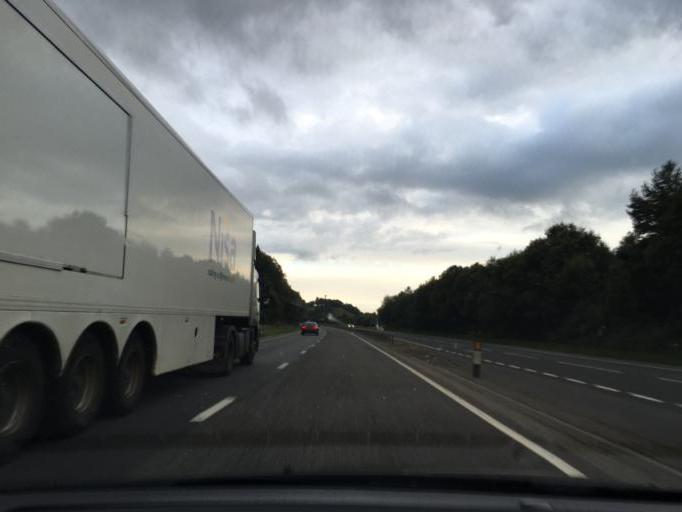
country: GB
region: Scotland
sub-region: Highland
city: Inverness
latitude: 57.4173
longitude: -4.1344
